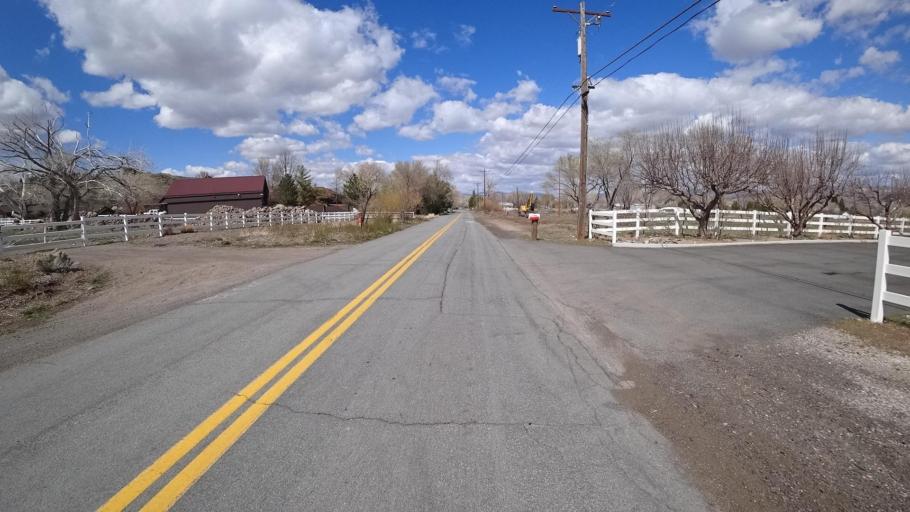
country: US
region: Nevada
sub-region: Washoe County
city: Reno
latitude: 39.4313
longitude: -119.7892
